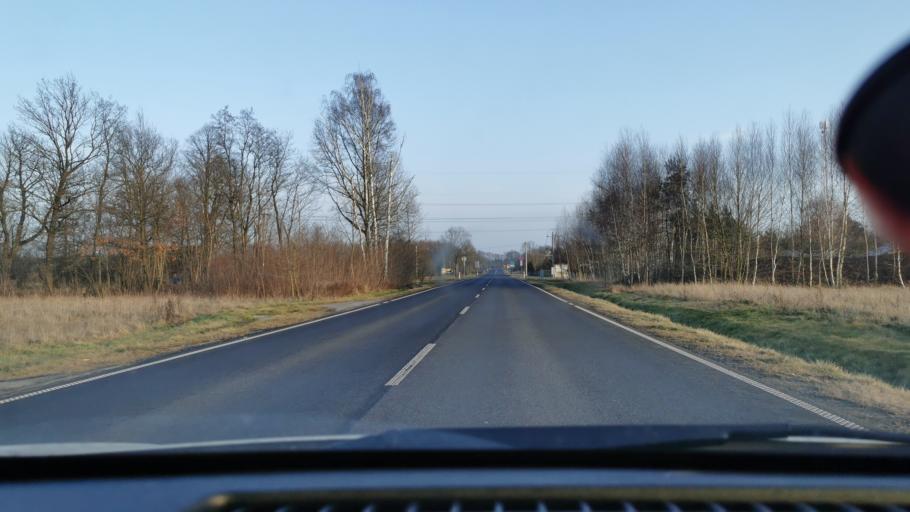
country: PL
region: Lodz Voivodeship
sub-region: Powiat belchatowski
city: Zelow
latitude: 51.5271
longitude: 19.2926
